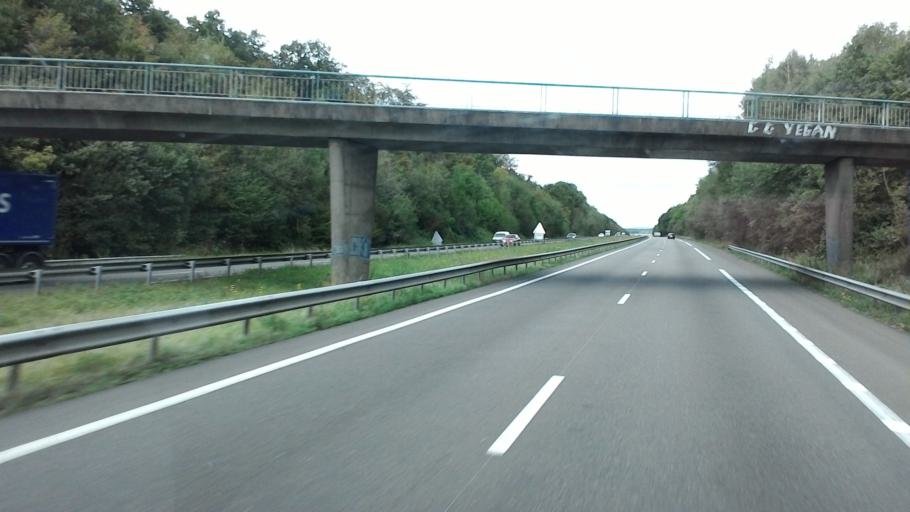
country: FR
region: Lorraine
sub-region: Departement de Meurthe-et-Moselle
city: Pont-a-Mousson
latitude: 48.9142
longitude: 6.1098
